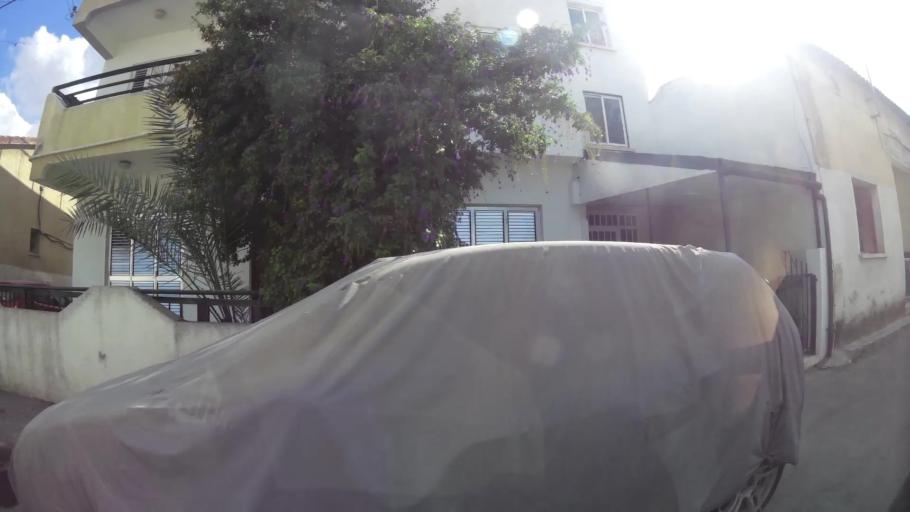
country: CY
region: Lefkosia
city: Nicosia
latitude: 35.1963
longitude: 33.3540
